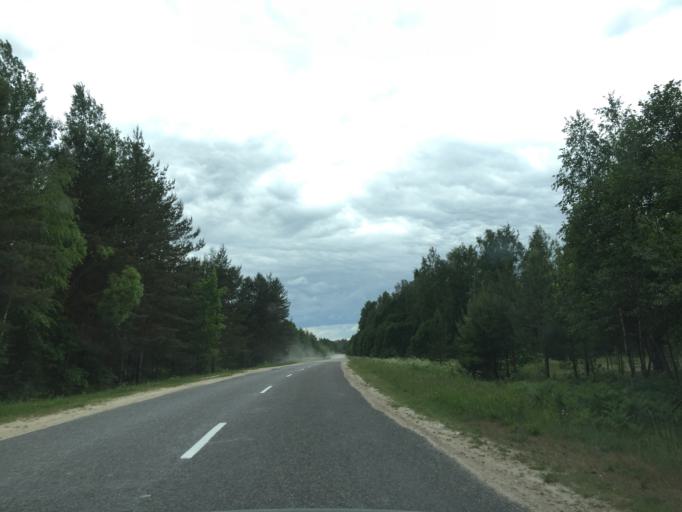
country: LV
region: Vilanu
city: Vilani
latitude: 56.4425
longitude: 27.0805
